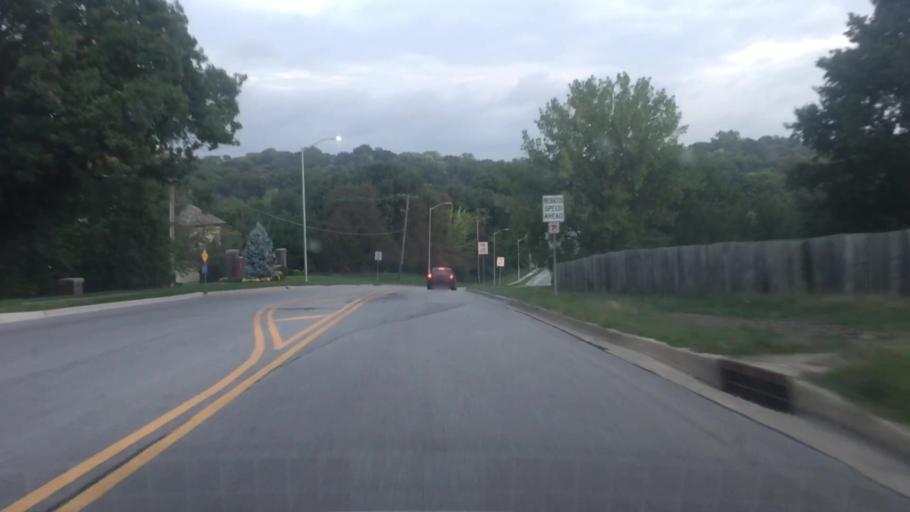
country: US
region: Kansas
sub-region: Johnson County
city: Shawnee
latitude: 39.0367
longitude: -94.7507
